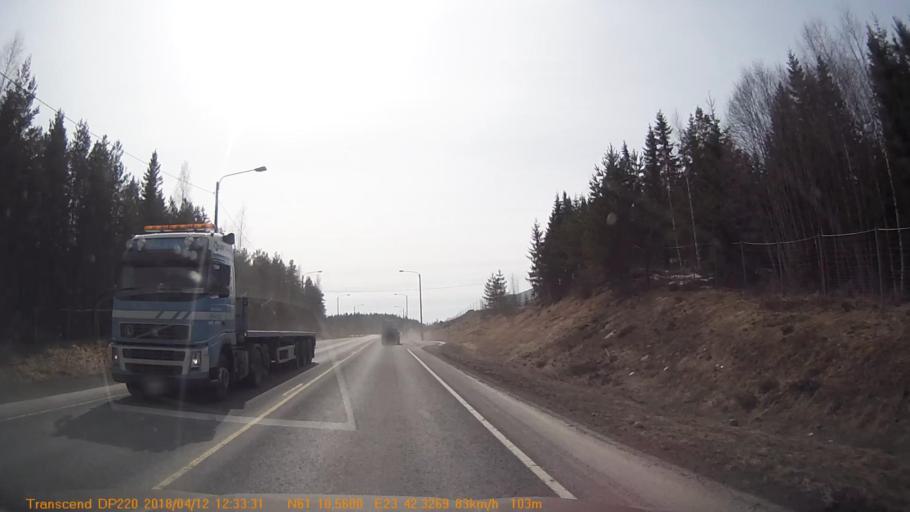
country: FI
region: Pirkanmaa
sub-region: Etelae-Pirkanmaa
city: Kylmaekoski
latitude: 61.1756
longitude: 23.7052
